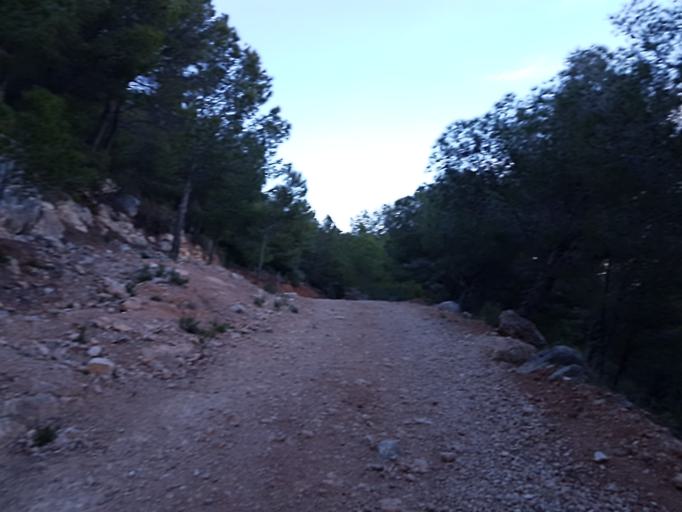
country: ES
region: Valencia
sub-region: Provincia de Alicante
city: Calp
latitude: 38.6512
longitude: 0.0234
